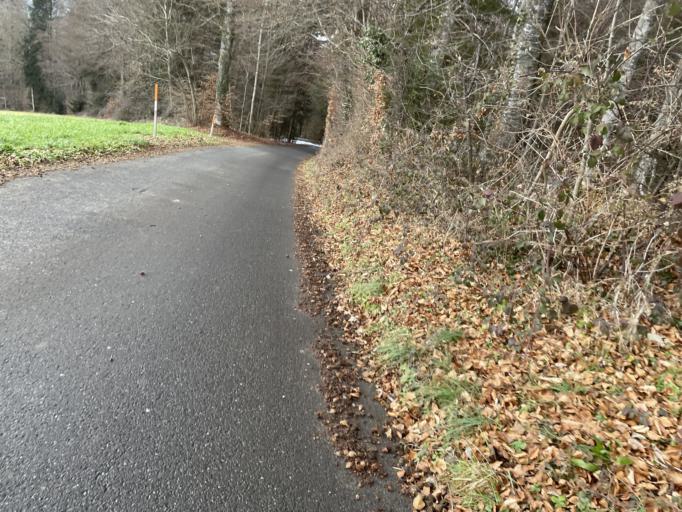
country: CH
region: Lucerne
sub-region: Entlebuch District
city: Oberdiessbach
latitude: 46.8430
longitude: 7.6046
